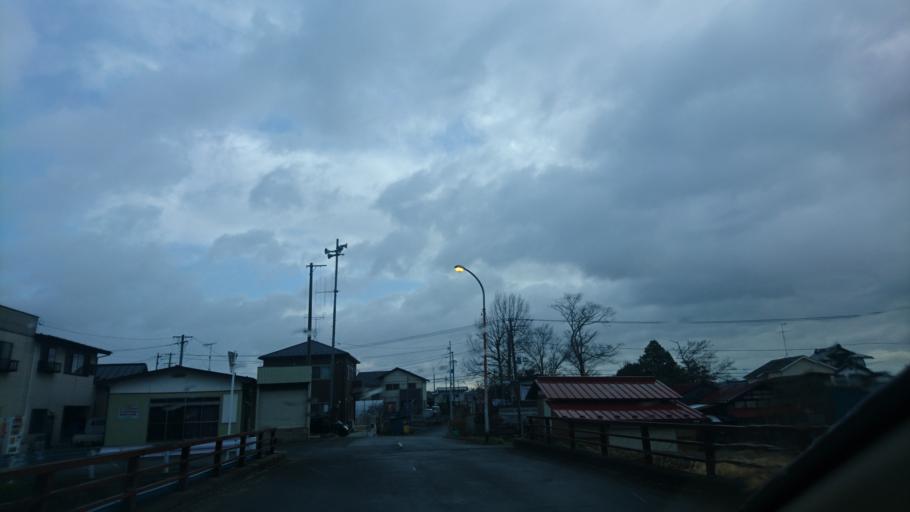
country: JP
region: Iwate
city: Ichinoseki
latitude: 38.7736
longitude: 141.0267
